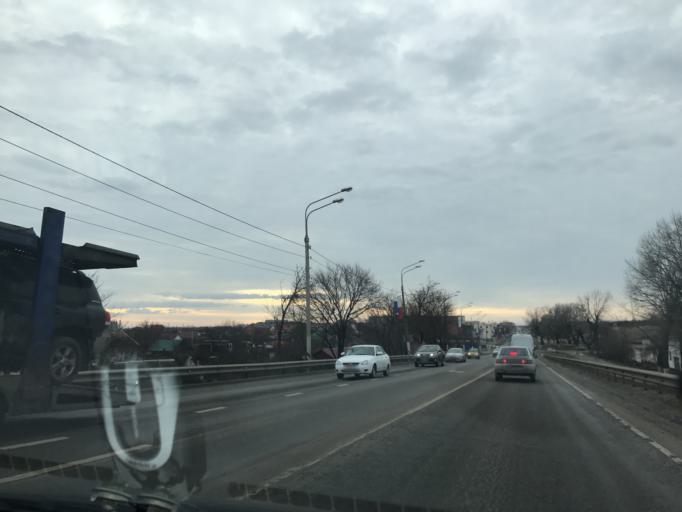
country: RU
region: Krasnodarskiy
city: Kropotkin
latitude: 45.4297
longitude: 40.5374
